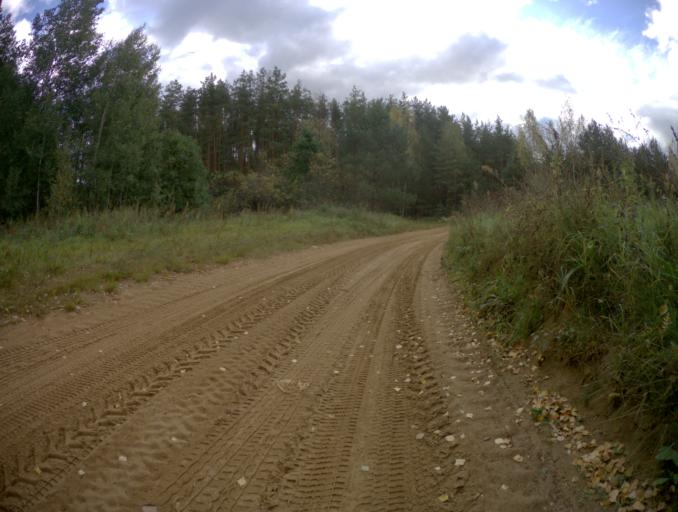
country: RU
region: Vladimir
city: Petushki
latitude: 55.8843
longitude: 39.5246
